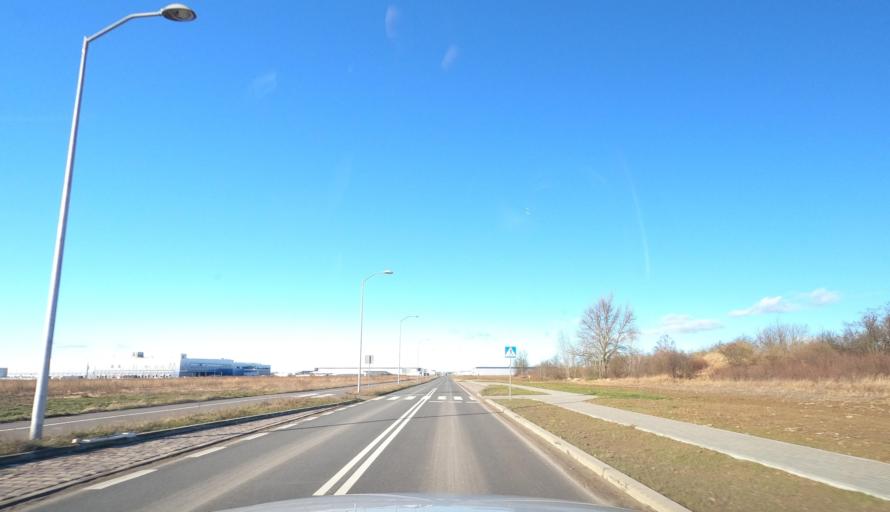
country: PL
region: West Pomeranian Voivodeship
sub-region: Powiat pyrzycki
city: Warnice
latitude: 53.2786
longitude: 14.9752
